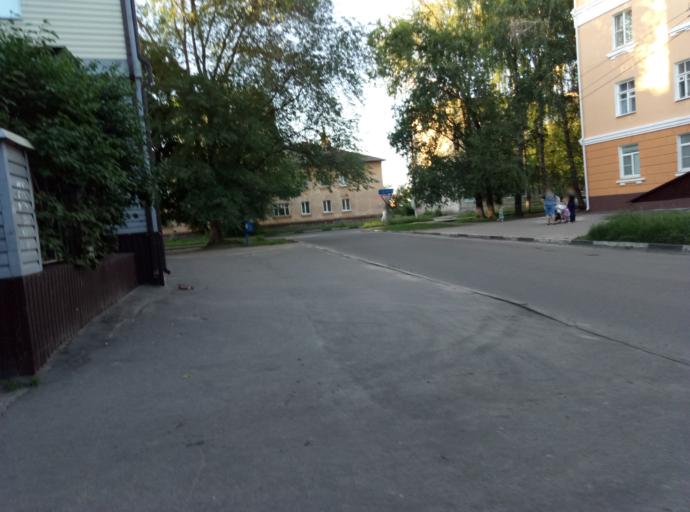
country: RU
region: Kursk
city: Kursk
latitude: 51.6738
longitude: 36.1526
